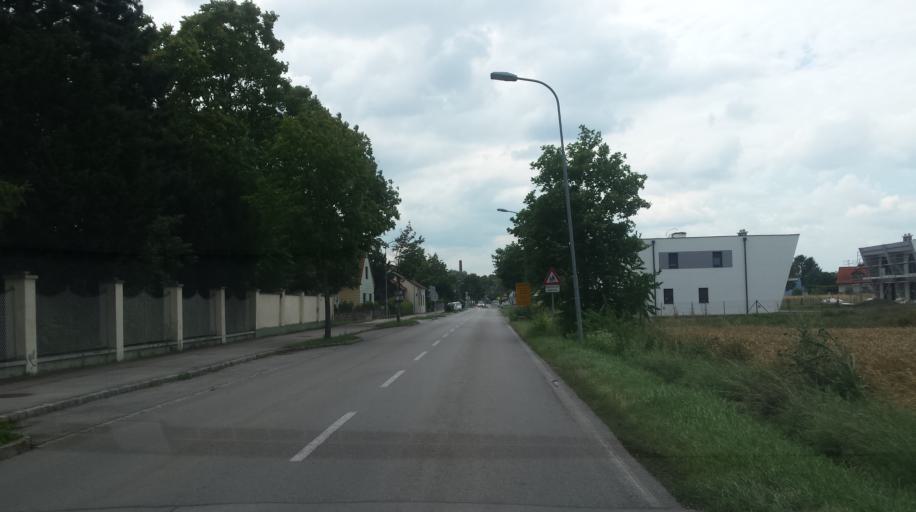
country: AT
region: Lower Austria
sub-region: Politischer Bezirk Baden
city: Ebreichsdorf
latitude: 47.9664
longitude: 16.4304
